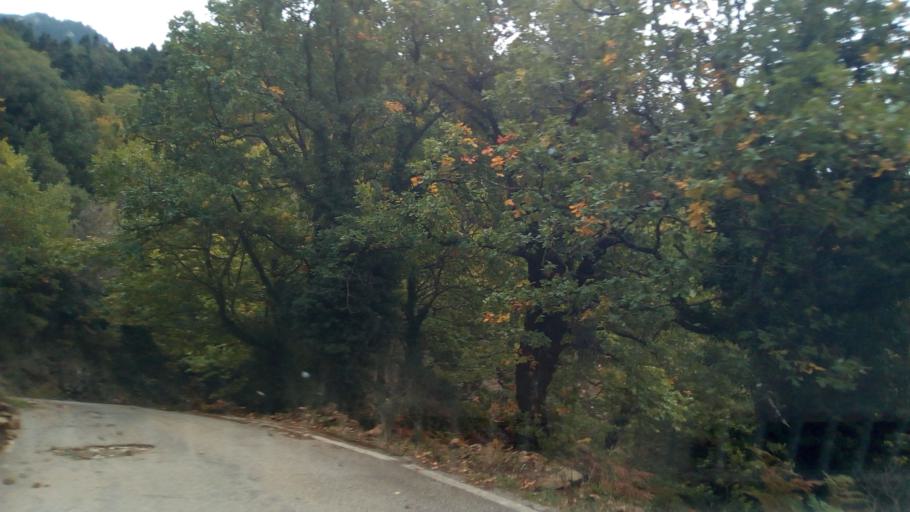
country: GR
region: West Greece
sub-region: Nomos Aitolias kai Akarnanias
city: Thermo
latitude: 38.5853
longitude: 21.8498
